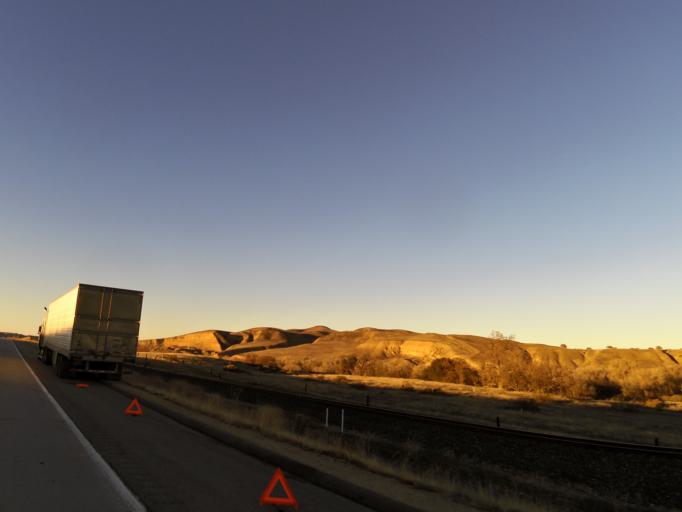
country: US
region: California
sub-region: San Luis Obispo County
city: San Miguel
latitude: 35.7902
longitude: -120.7309
